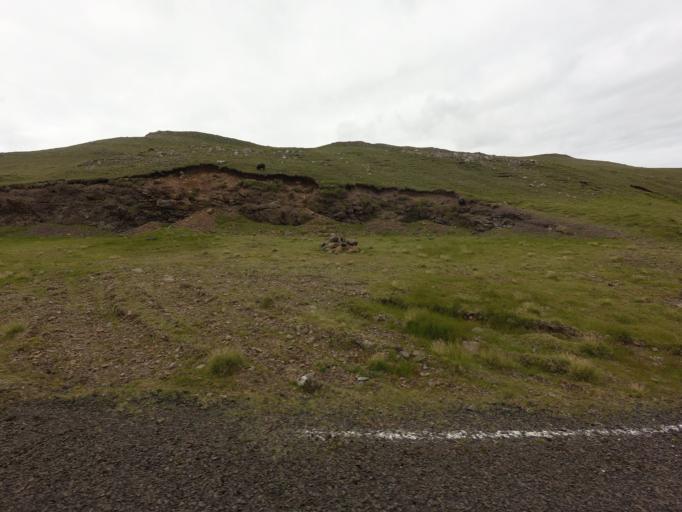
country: FO
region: Suduroy
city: Vagur
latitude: 61.4395
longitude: -6.7492
